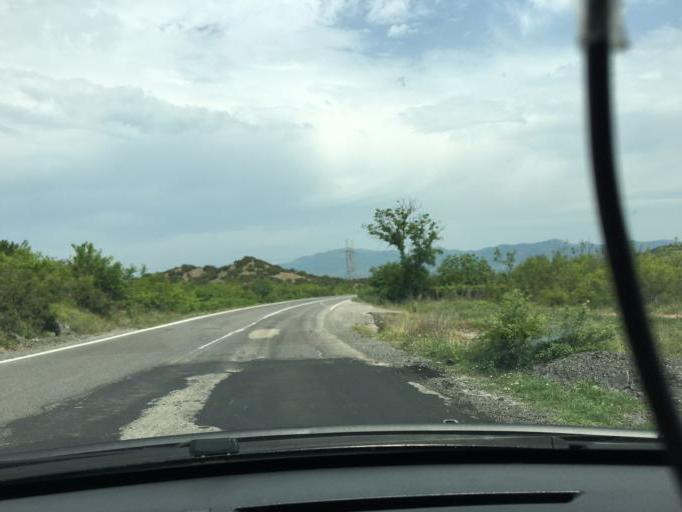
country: MK
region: Gevgelija
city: Miravci
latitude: 41.2661
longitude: 22.4760
